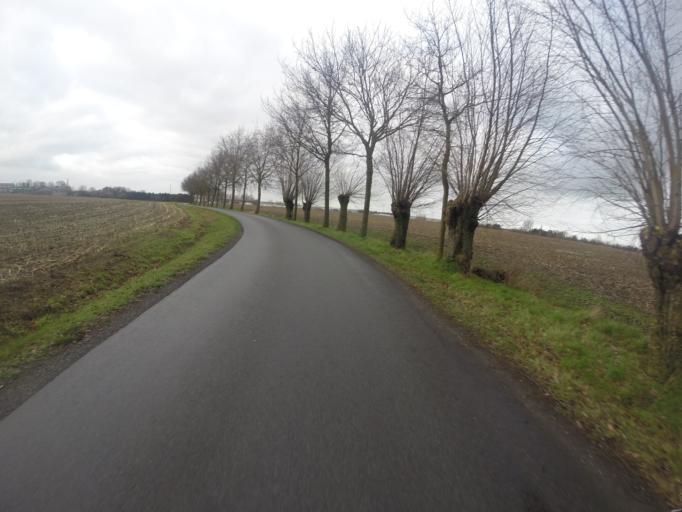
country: BE
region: Flanders
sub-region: Provincie Oost-Vlaanderen
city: Maldegem
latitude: 51.1885
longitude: 3.4766
